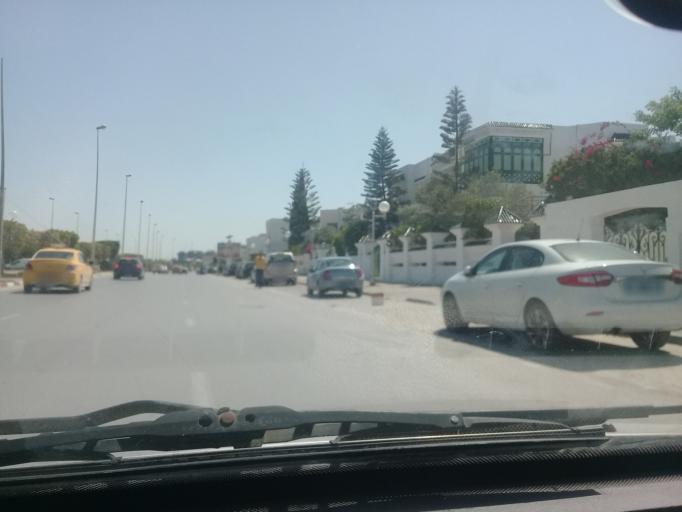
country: TN
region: Ariana
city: Ariana
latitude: 36.8396
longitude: 10.2469
